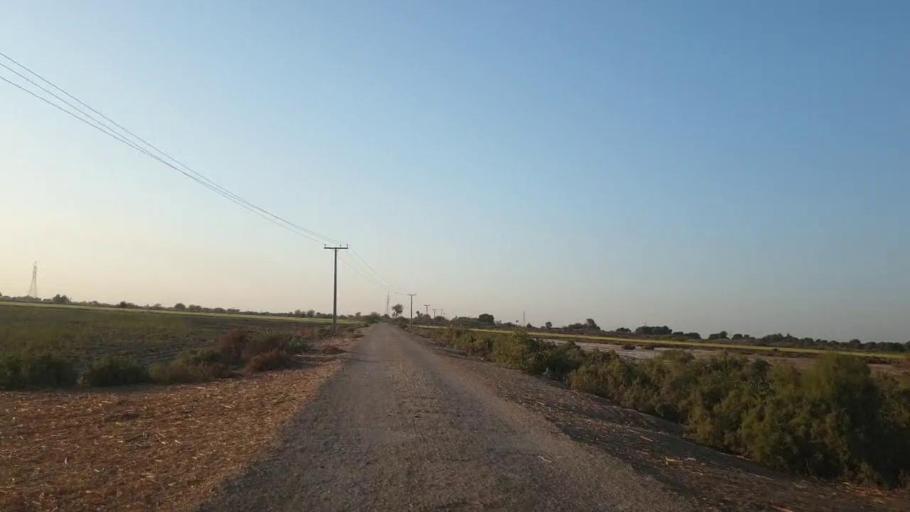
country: PK
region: Sindh
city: Mirpur Khas
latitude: 25.6987
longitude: 69.0455
